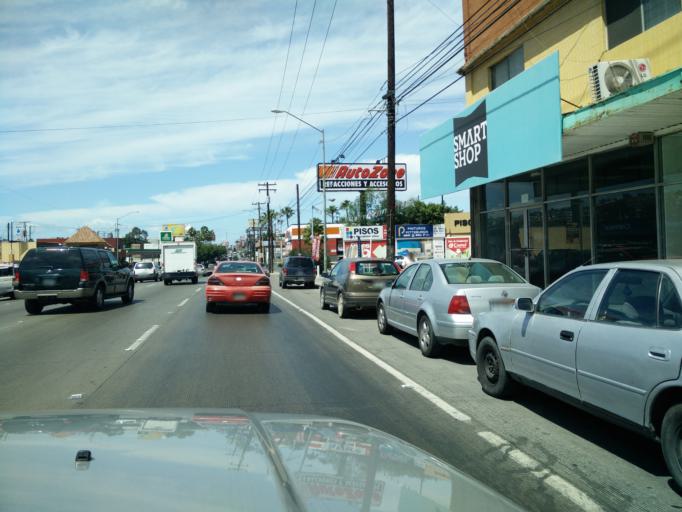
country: MX
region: Baja California
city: Tijuana
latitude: 32.5162
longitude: -117.0117
